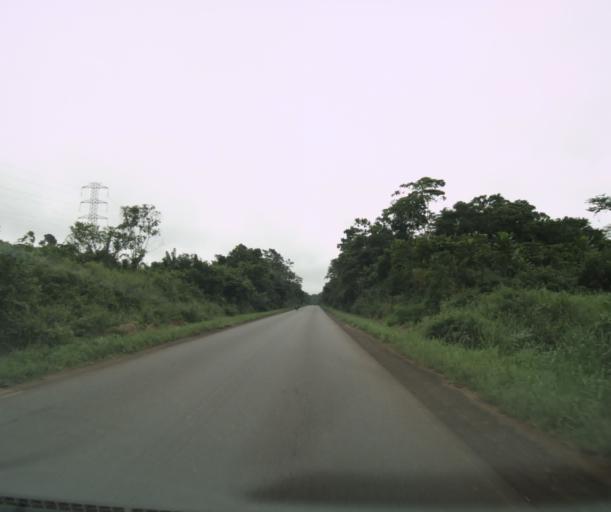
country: CM
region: Littoral
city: Edea
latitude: 3.6753
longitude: 10.1099
